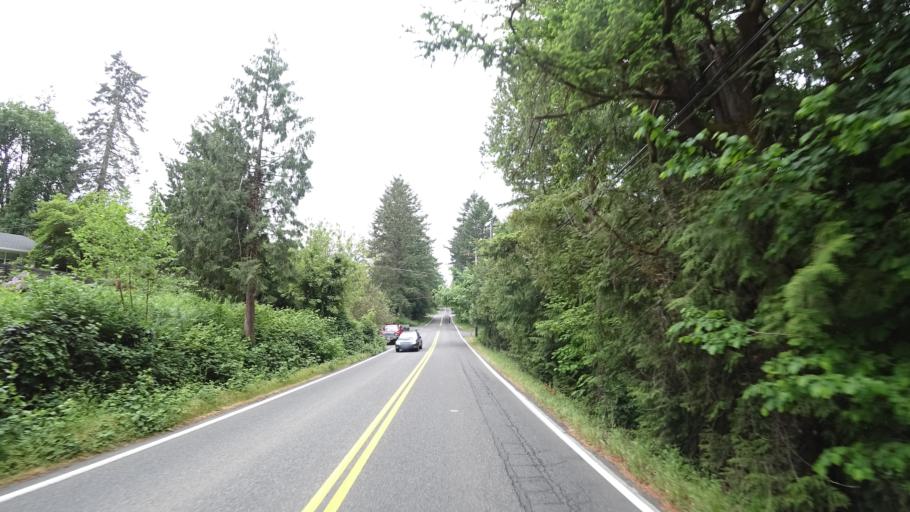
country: US
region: Oregon
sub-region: Washington County
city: Raleigh Hills
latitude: 45.4764
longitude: -122.7407
